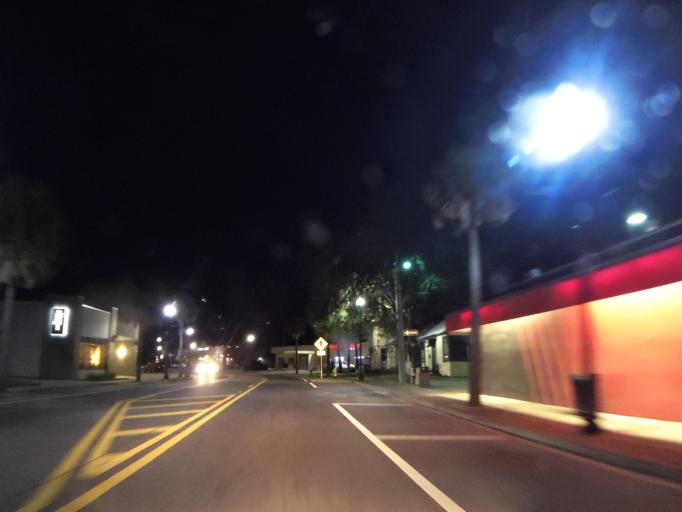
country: US
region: Florida
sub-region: Duval County
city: Jacksonville
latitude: 30.3082
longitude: -81.6605
